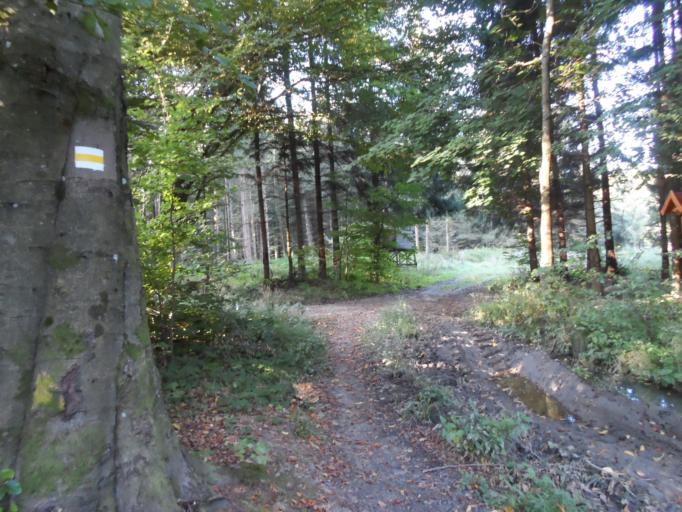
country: HU
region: Veszprem
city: Zirc
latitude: 47.2791
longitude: 17.7822
